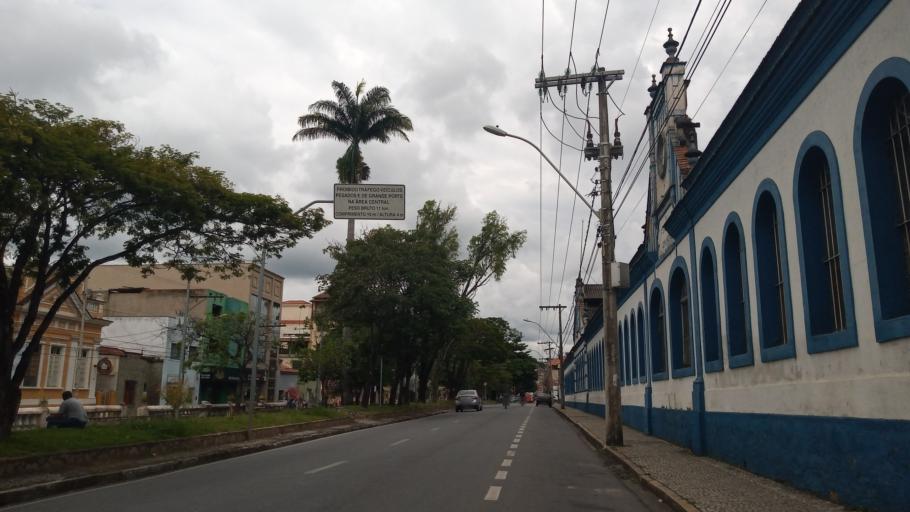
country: BR
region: Minas Gerais
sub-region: Sao Joao Del Rei
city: Sao Joao del Rei
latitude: -21.1265
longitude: -44.2492
